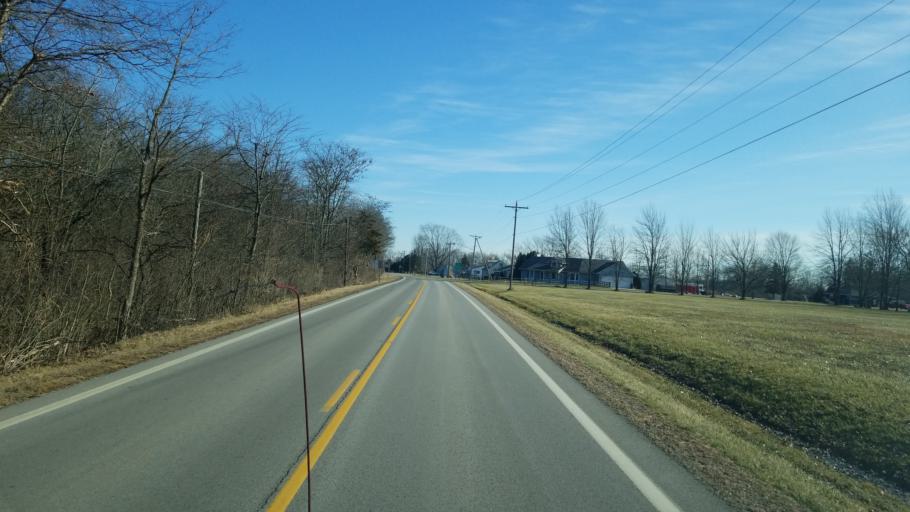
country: US
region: Ohio
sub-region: Wood County
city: Weston
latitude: 41.4101
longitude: -83.8847
